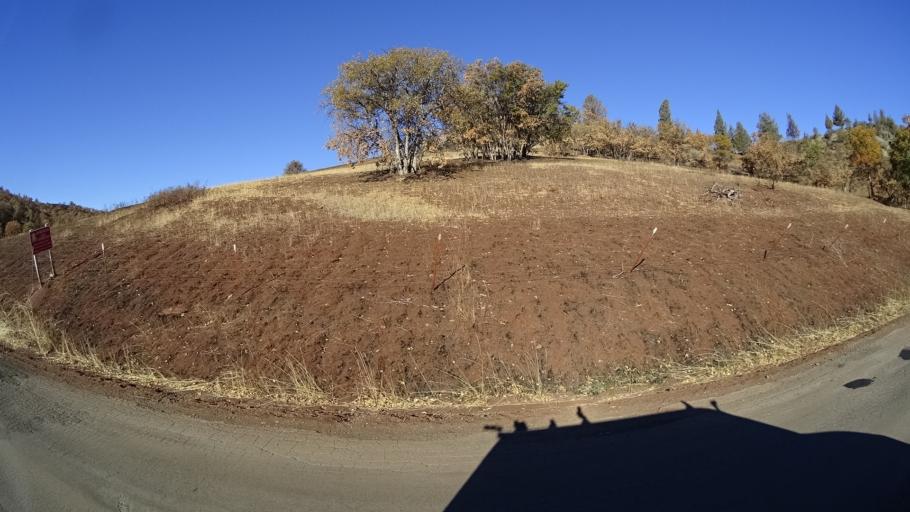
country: US
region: California
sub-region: Siskiyou County
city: Montague
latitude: 41.9133
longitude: -122.4620
